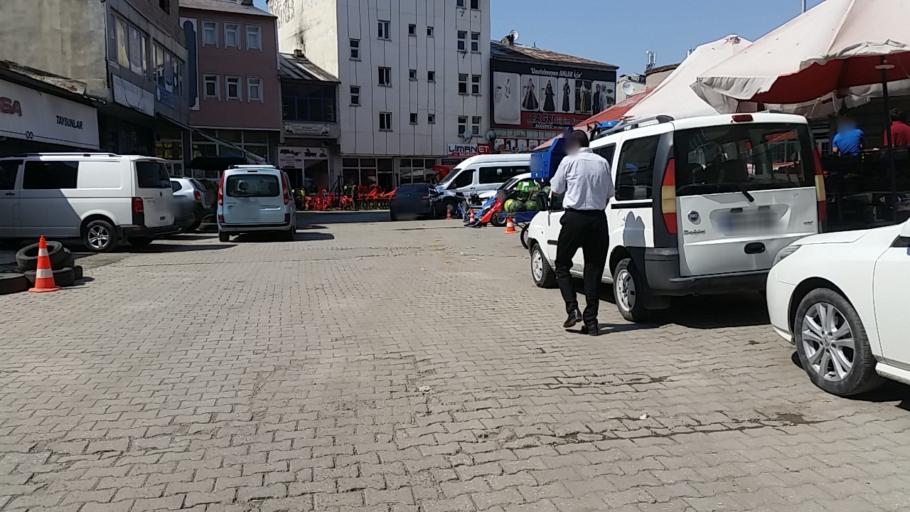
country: TR
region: Agri
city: Agri
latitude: 39.7151
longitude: 43.0522
